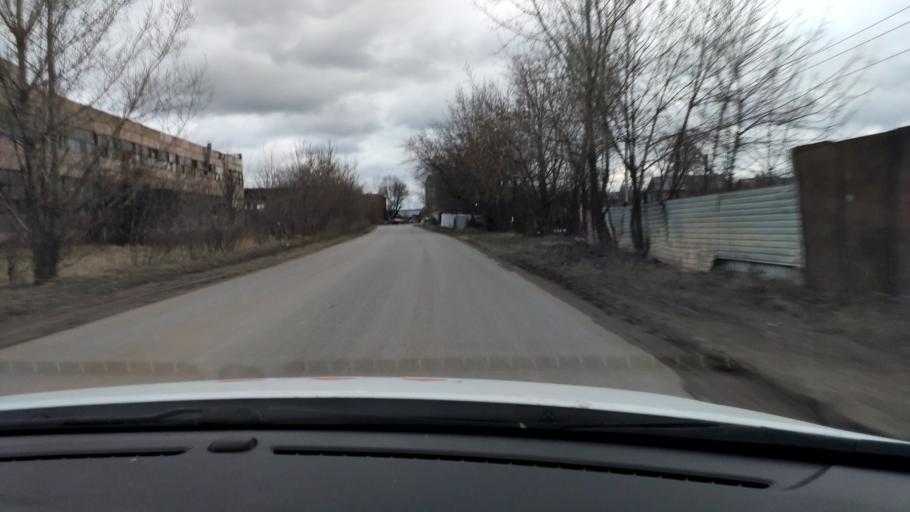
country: RU
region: Tatarstan
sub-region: Gorod Kazan'
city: Kazan
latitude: 55.7214
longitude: 49.0927
